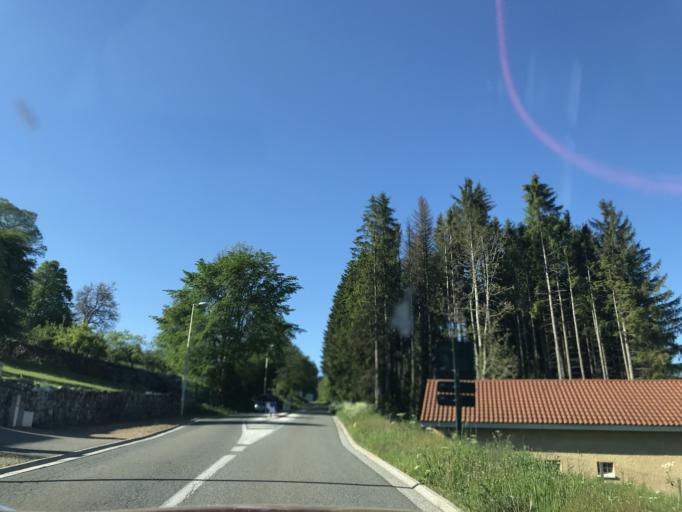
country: FR
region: Auvergne
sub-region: Departement du Puy-de-Dome
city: Cunlhat
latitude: 45.5735
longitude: 3.6302
